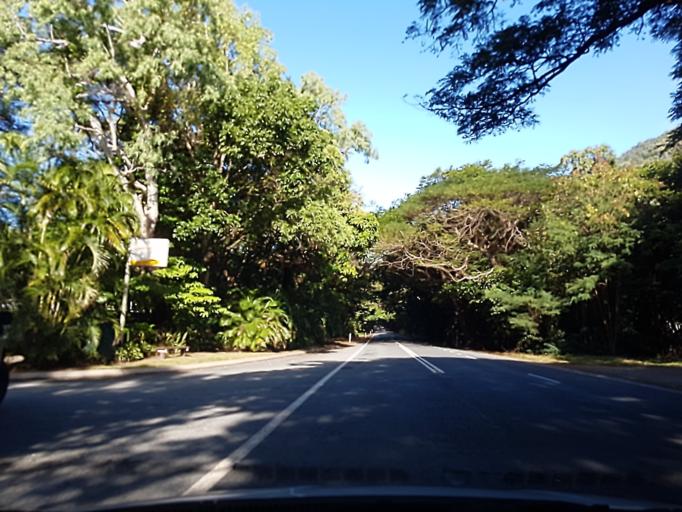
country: AU
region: Queensland
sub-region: Cairns
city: Palm Cove
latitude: -16.7265
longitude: 145.6466
